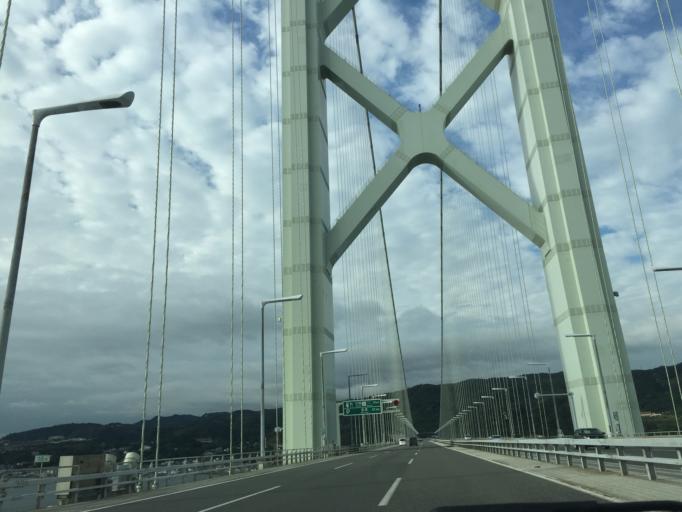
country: JP
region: Hyogo
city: Akashi
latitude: 34.6102
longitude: 135.0154
